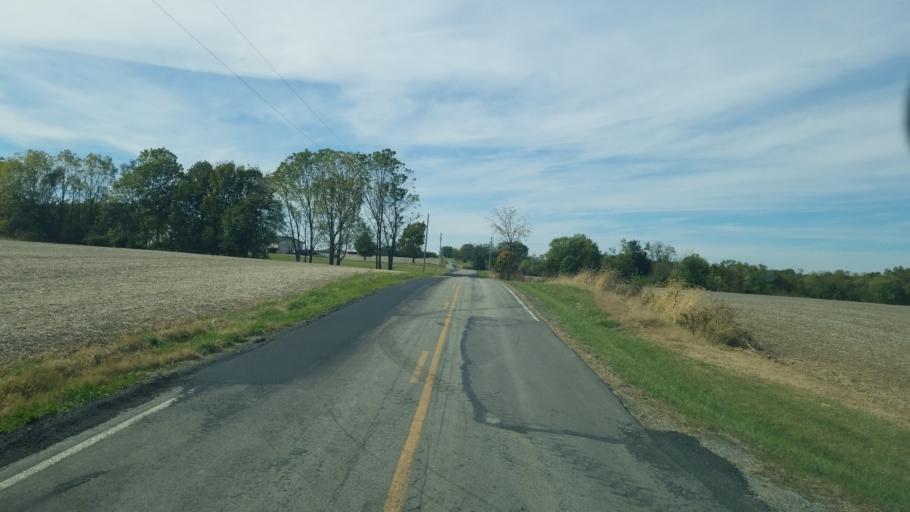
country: US
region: Ohio
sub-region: Highland County
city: Leesburg
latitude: 39.3296
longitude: -83.4915
